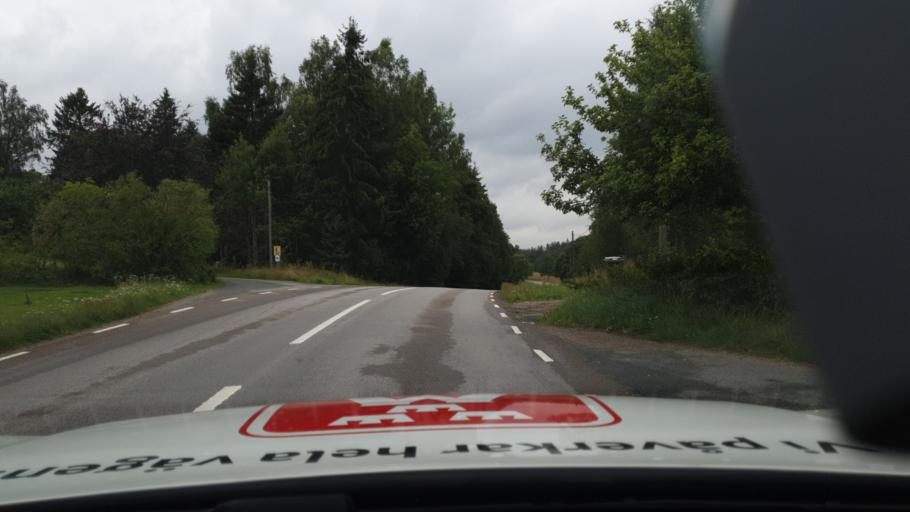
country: SE
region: Vaestra Goetaland
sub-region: Lilla Edets Kommun
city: Lilla Edet
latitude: 58.1472
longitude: 12.0777
